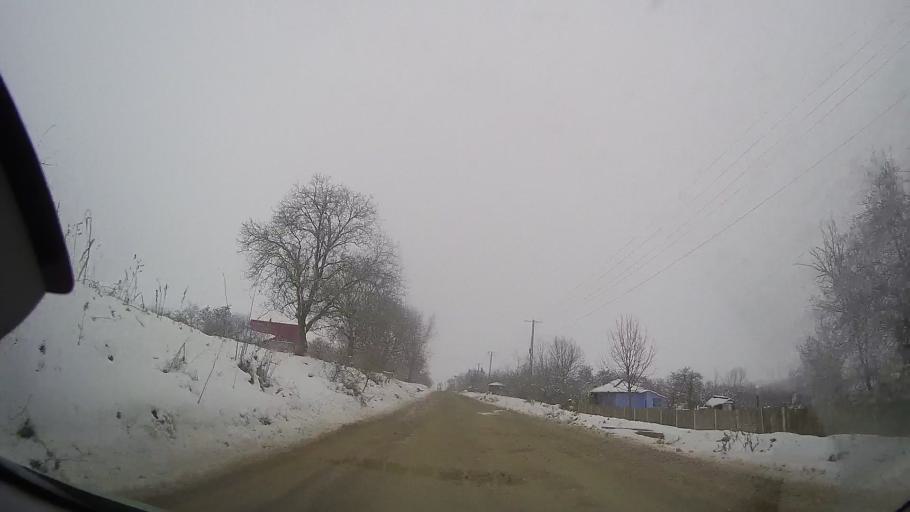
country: RO
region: Vaslui
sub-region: Comuna Todiresti
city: Todiresti
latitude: 46.8756
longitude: 27.3769
